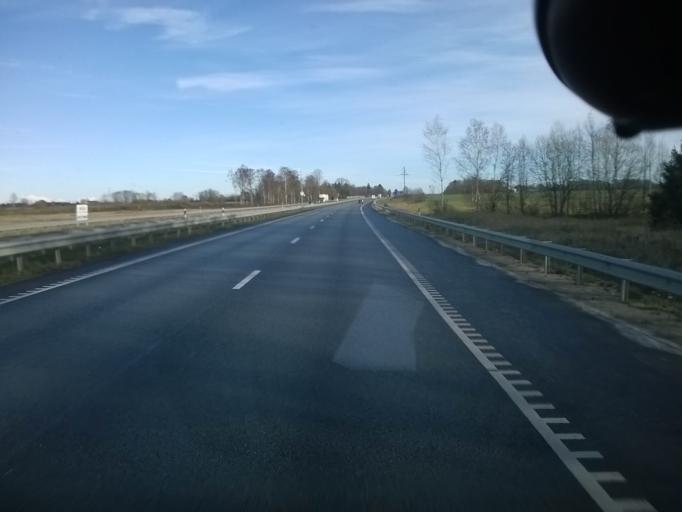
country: EE
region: Harju
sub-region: Kiili vald
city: Kiili
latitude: 59.3328
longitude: 24.8002
